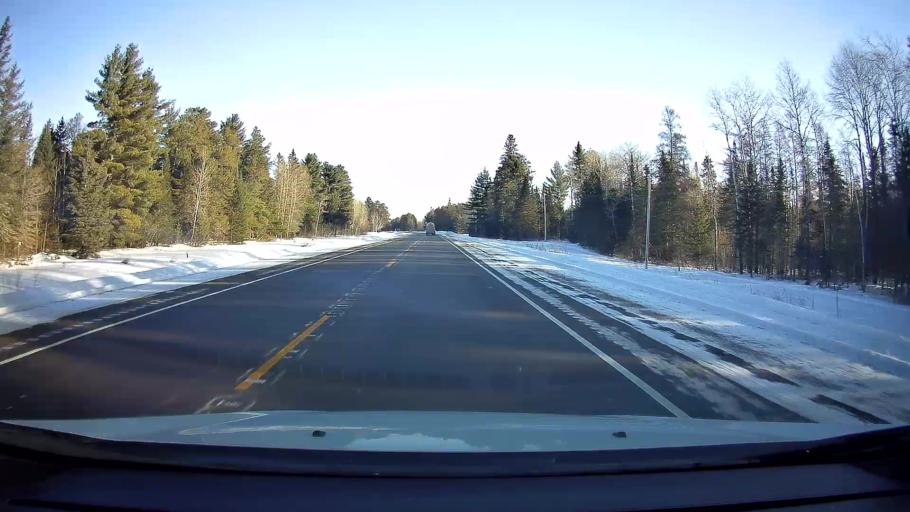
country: US
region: Wisconsin
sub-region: Sawyer County
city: Hayward
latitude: 46.0818
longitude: -91.4005
